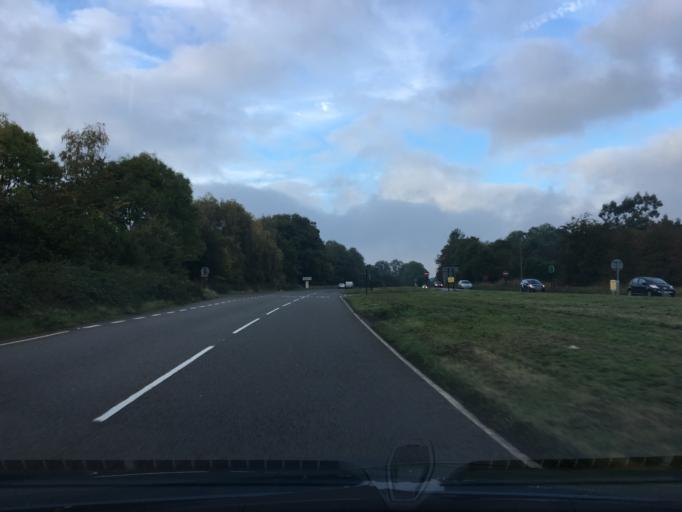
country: GB
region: England
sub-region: Hampshire
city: Long Sutton
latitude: 51.1730
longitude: -0.9206
